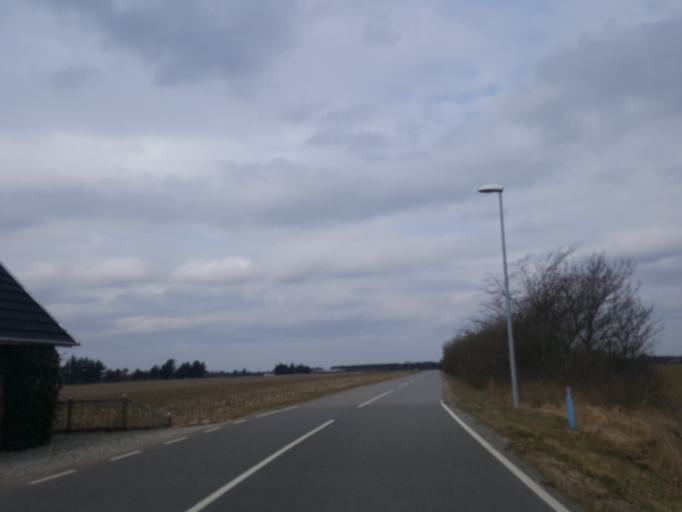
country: DK
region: Central Jutland
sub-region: Holstebro Kommune
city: Ulfborg
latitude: 56.3394
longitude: 8.3070
